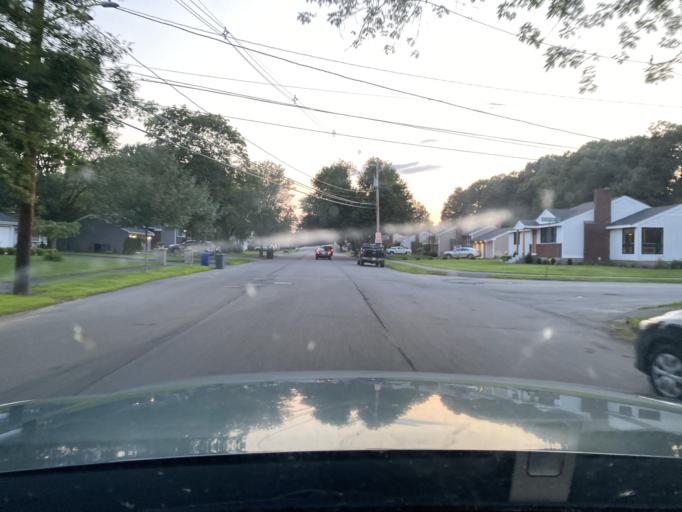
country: US
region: Massachusetts
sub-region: Essex County
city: Lynnfield
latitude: 42.5369
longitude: -70.9990
